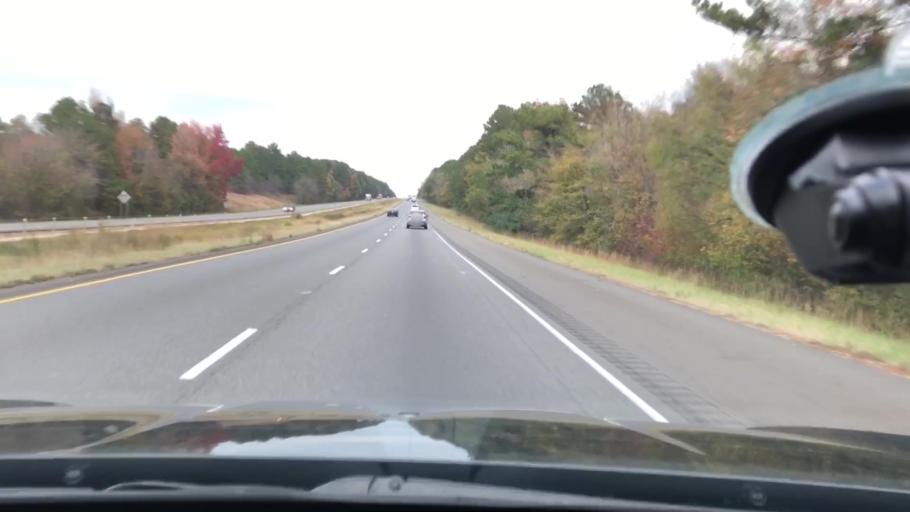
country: US
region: Arkansas
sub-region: Clark County
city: Arkadelphia
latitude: 34.2638
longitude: -92.9780
